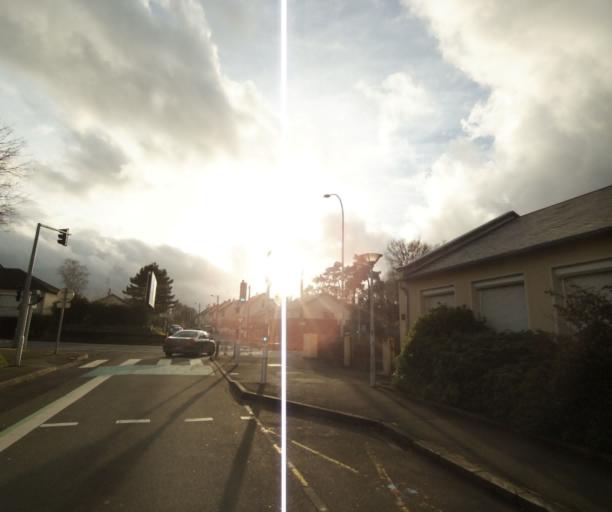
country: FR
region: Pays de la Loire
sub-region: Departement de la Sarthe
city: Le Mans
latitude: 47.9779
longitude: 0.2302
